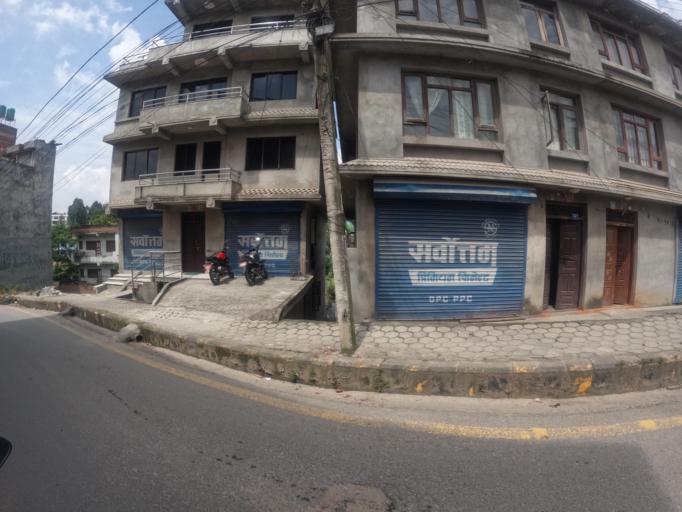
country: NP
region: Central Region
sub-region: Bagmati Zone
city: Bhaktapur
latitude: 27.6818
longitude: 85.3834
